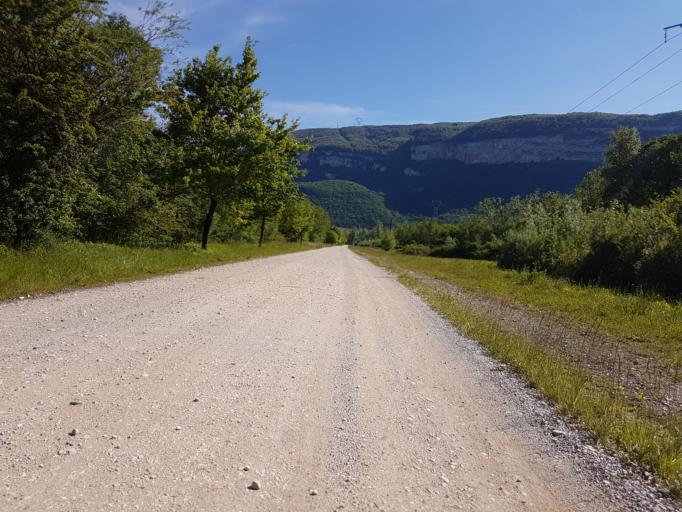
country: FR
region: Rhone-Alpes
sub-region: Departement de l'Isere
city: Montalieu-Vercieu
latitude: 45.8188
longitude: 5.4314
